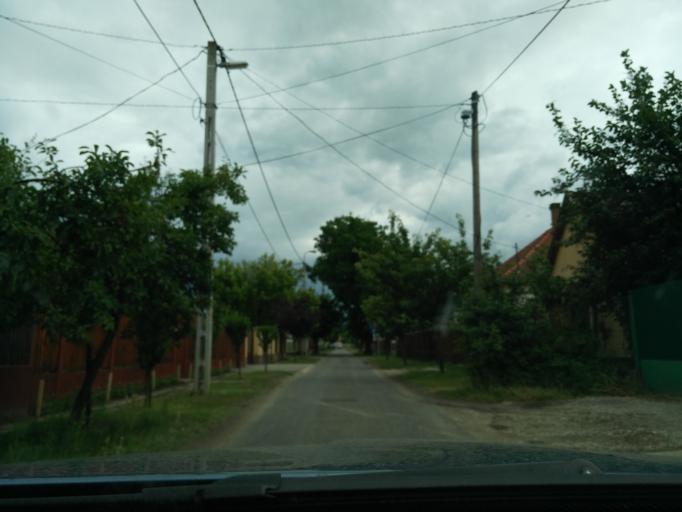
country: HU
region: Hajdu-Bihar
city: Debrecen
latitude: 47.5498
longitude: 21.6562
